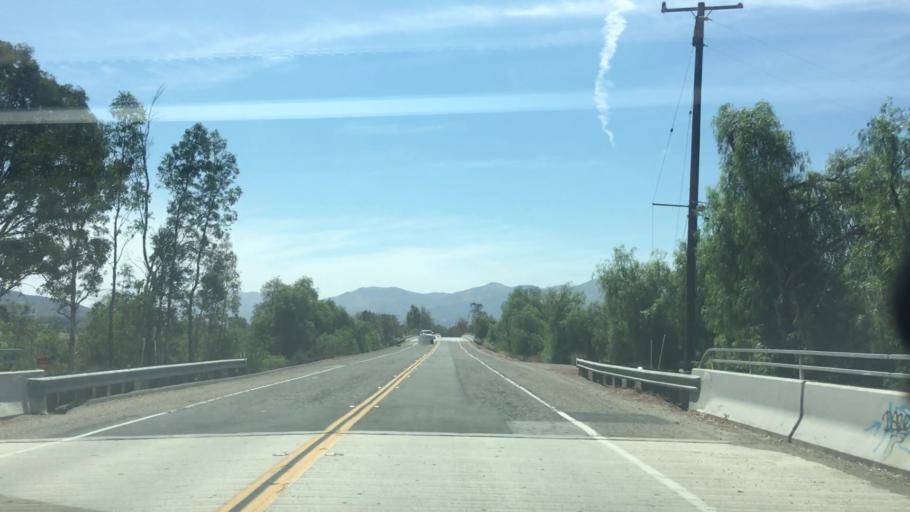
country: US
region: California
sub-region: Ventura County
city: Fillmore
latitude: 34.4070
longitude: -118.9337
